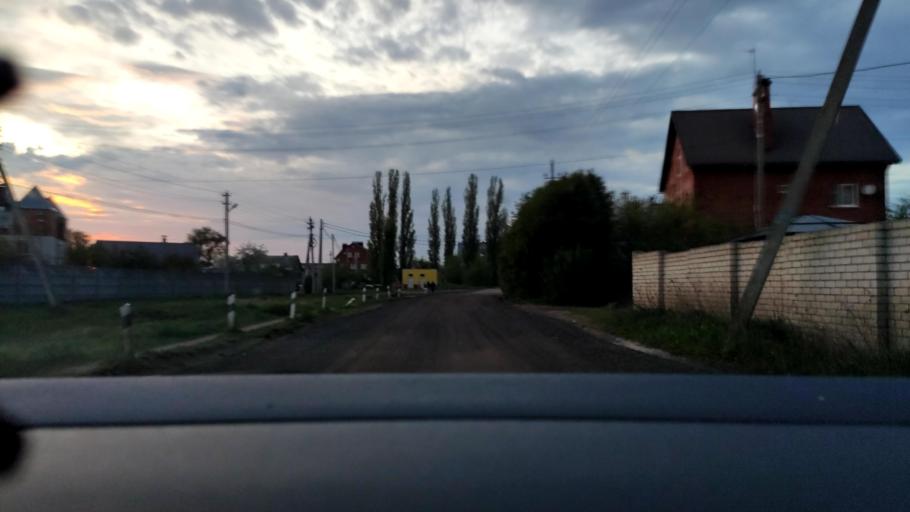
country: RU
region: Voronezj
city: Podgornoye
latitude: 51.7380
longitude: 39.1642
